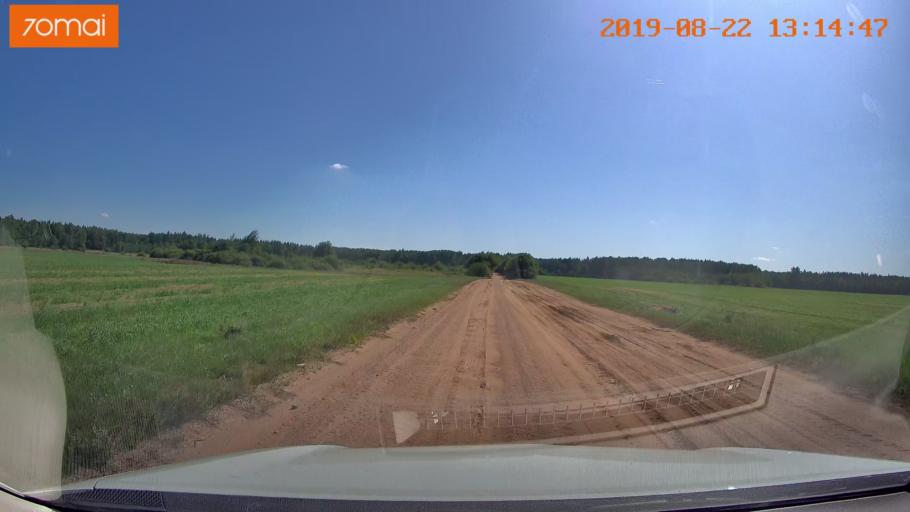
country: BY
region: Minsk
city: Prawdzinski
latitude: 53.2649
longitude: 27.8908
